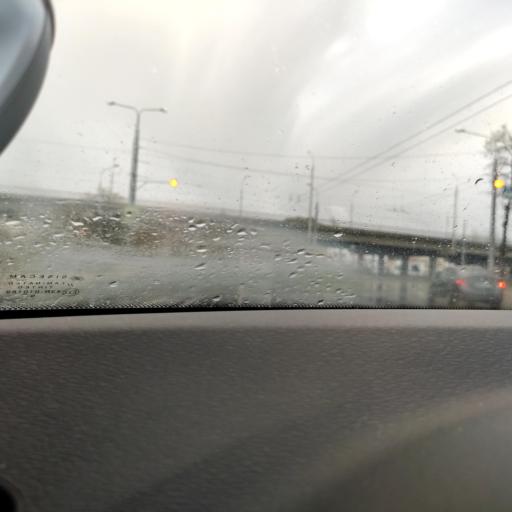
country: RU
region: Samara
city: Smyshlyayevka
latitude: 53.2080
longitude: 50.2762
